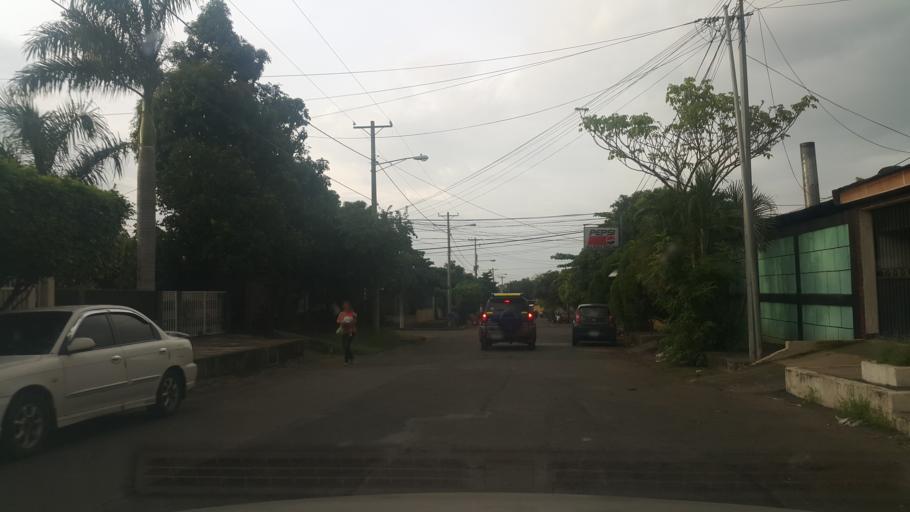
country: NI
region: Managua
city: Managua
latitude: 12.1311
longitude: -86.2976
